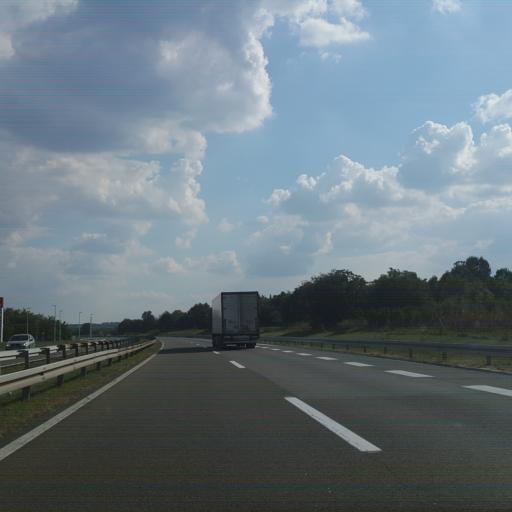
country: RS
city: Lugavcina
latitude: 44.5498
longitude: 20.9853
